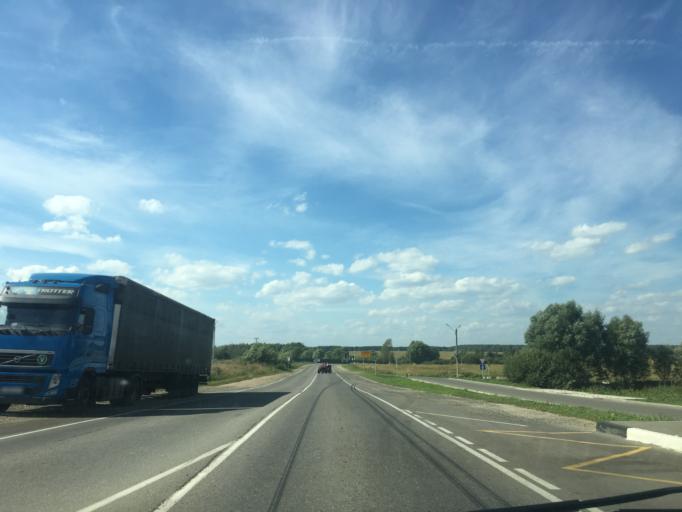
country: RU
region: Moskovskaya
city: Yam
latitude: 55.4767
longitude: 37.6665
